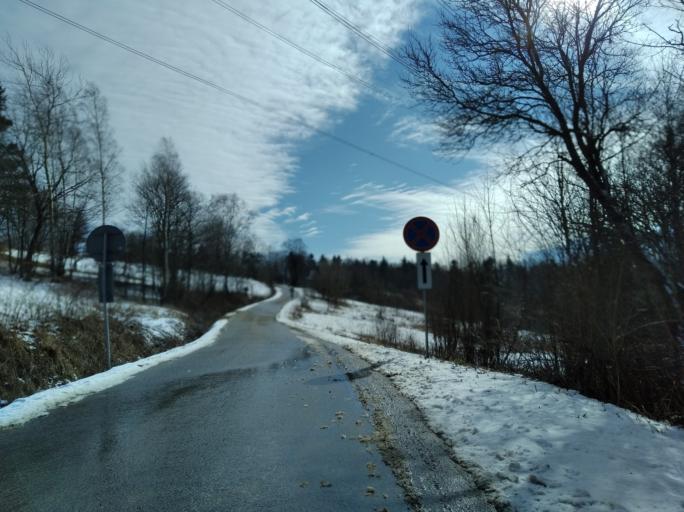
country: PL
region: Subcarpathian Voivodeship
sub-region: Powiat brzozowski
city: Jablonica Polska
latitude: 49.7309
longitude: 21.8957
